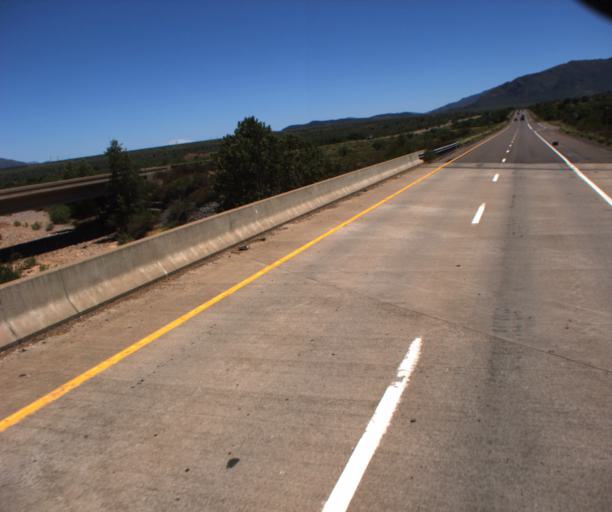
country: US
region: Arizona
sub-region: Gila County
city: Payson
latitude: 34.0865
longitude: -111.3551
